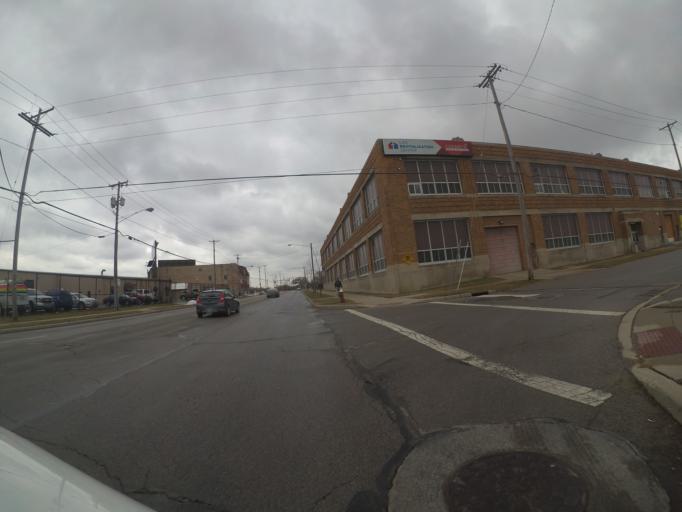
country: US
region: Ohio
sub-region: Lucas County
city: Toledo
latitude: 41.6521
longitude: -83.5479
